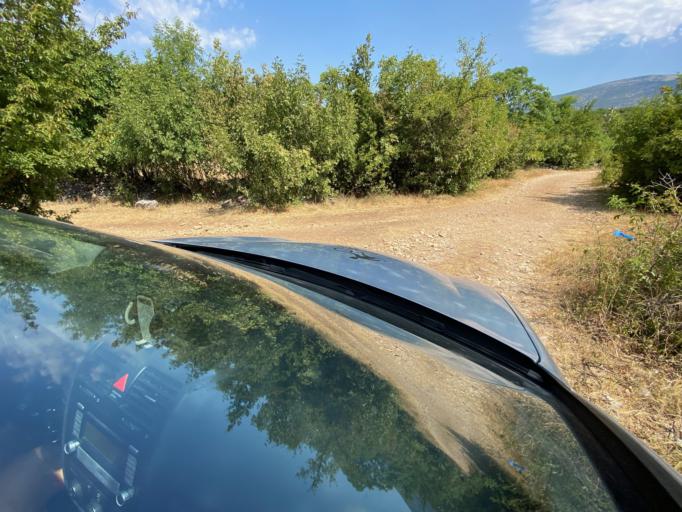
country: BA
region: Federation of Bosnia and Herzegovina
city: Bosansko Grahovo
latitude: 43.9525
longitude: 16.4382
